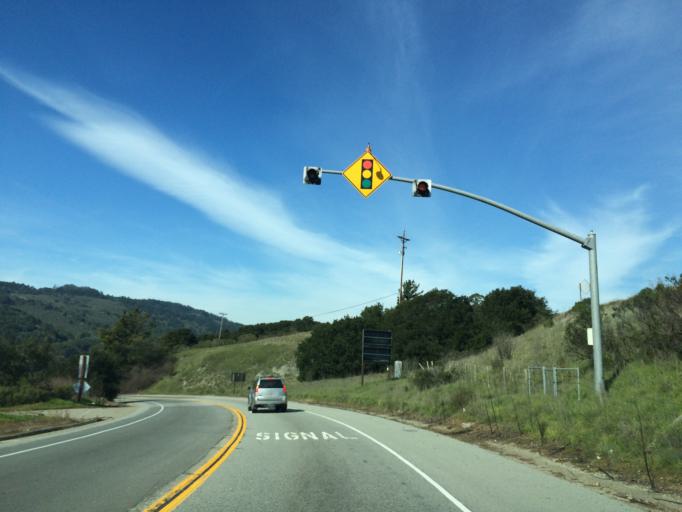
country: US
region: California
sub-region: San Mateo County
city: Highlands-Baywood Park
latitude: 37.5118
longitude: -122.3469
